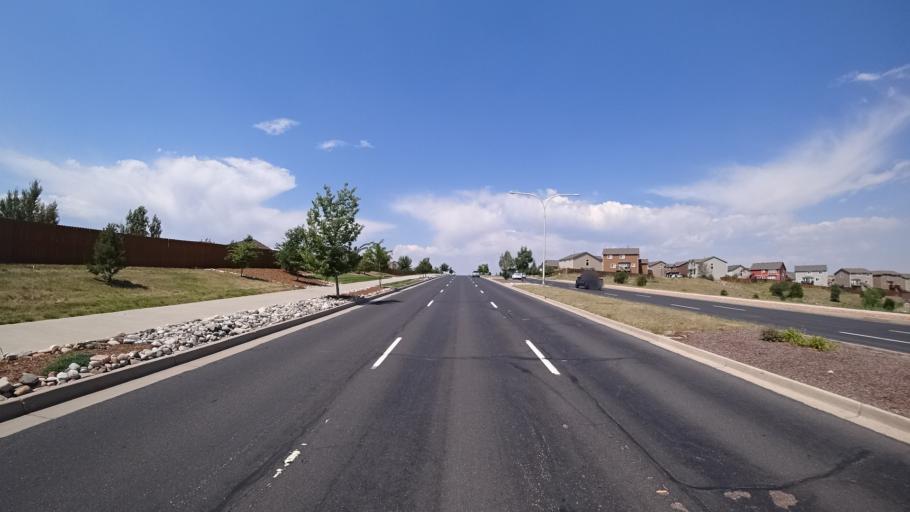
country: US
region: Colorado
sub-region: El Paso County
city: Cimarron Hills
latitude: 38.9260
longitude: -104.7046
